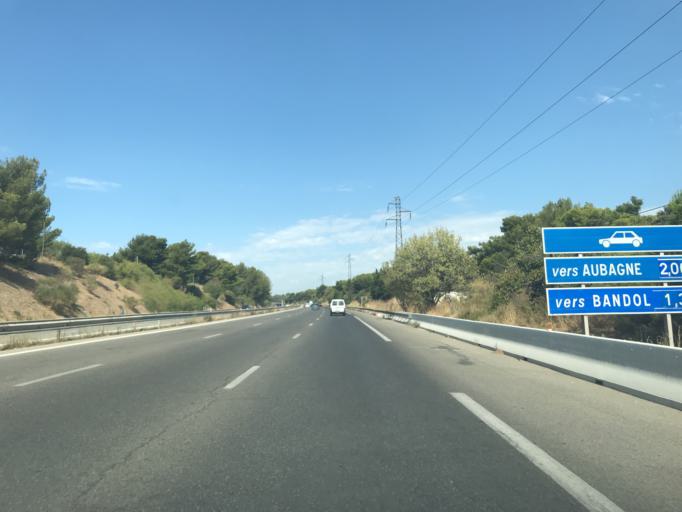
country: FR
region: Provence-Alpes-Cote d'Azur
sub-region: Departement du Var
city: Sanary-sur-Mer
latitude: 43.1351
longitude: 5.8090
